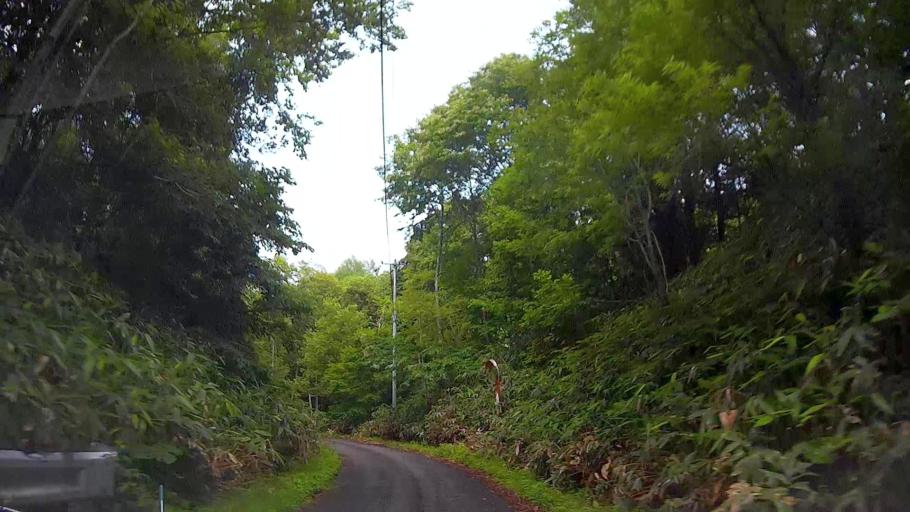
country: JP
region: Hokkaido
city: Nanae
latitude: 42.1028
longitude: 140.4536
